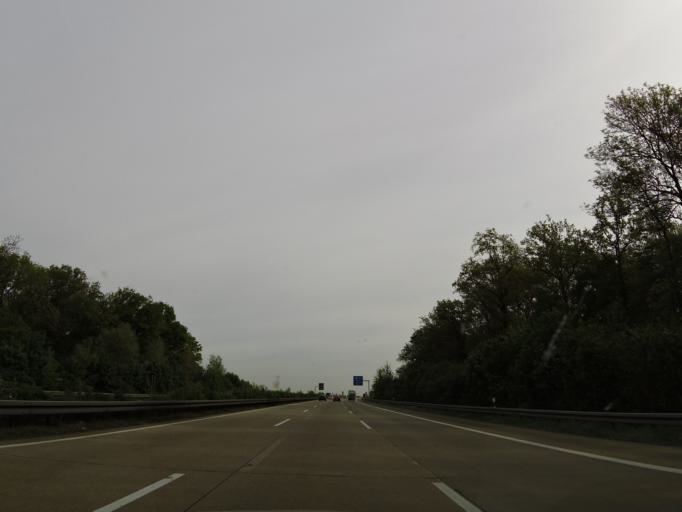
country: DE
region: Lower Saxony
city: Laatzen
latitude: 52.3449
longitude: 9.8694
